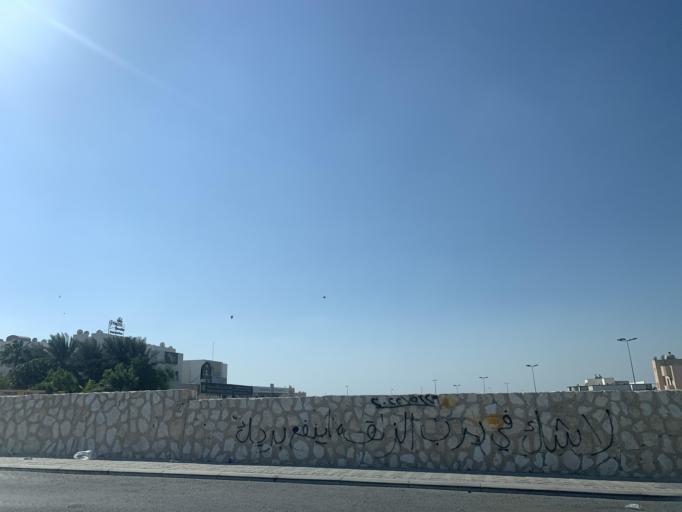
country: BH
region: Central Governorate
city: Madinat Hamad
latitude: 26.1204
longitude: 50.5057
